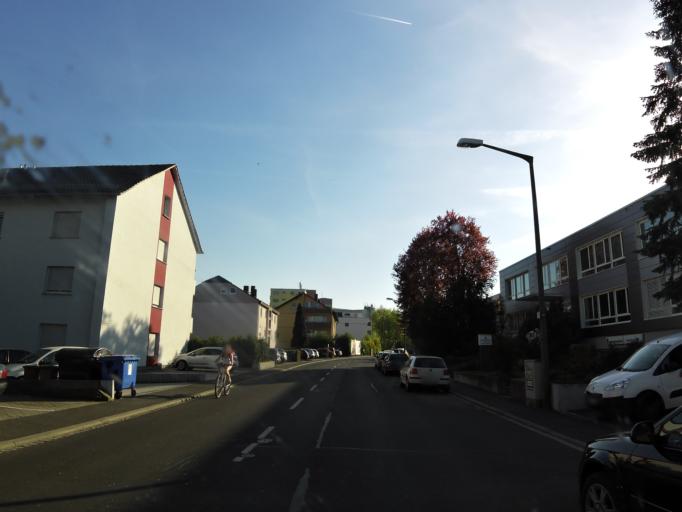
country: DE
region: Bavaria
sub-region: Regierungsbezirk Unterfranken
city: Estenfeld
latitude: 49.8132
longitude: 9.9805
